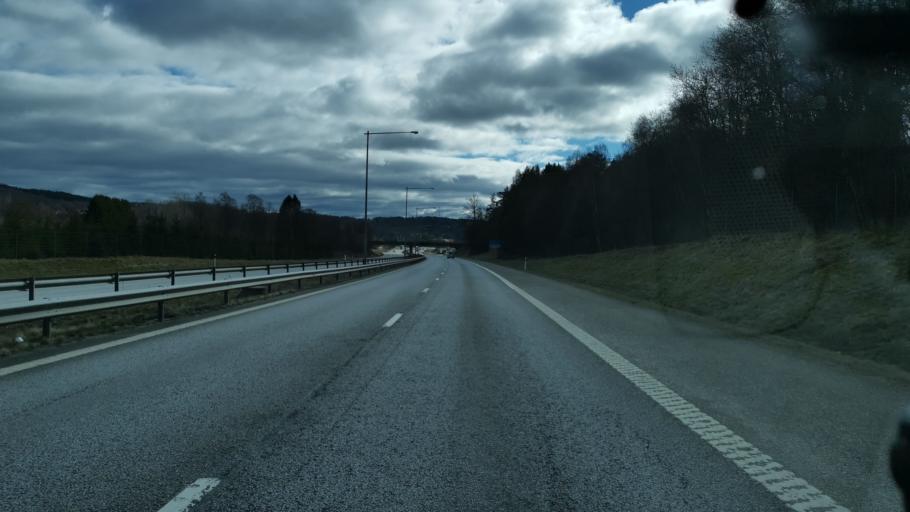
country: SE
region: Vaestra Goetaland
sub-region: Uddevalla Kommun
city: Ljungskile
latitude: 58.2354
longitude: 11.9114
